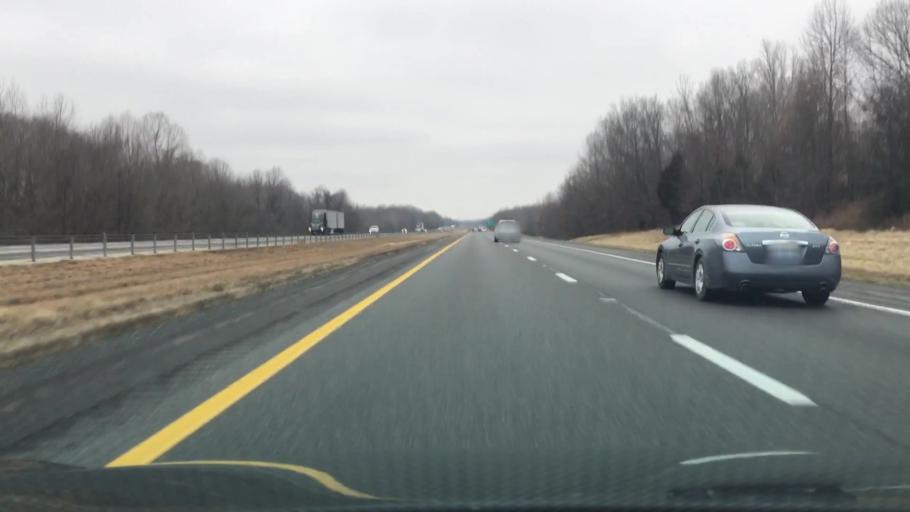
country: US
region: Kentucky
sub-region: McCracken County
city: Reidland
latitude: 36.9990
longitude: -88.5445
